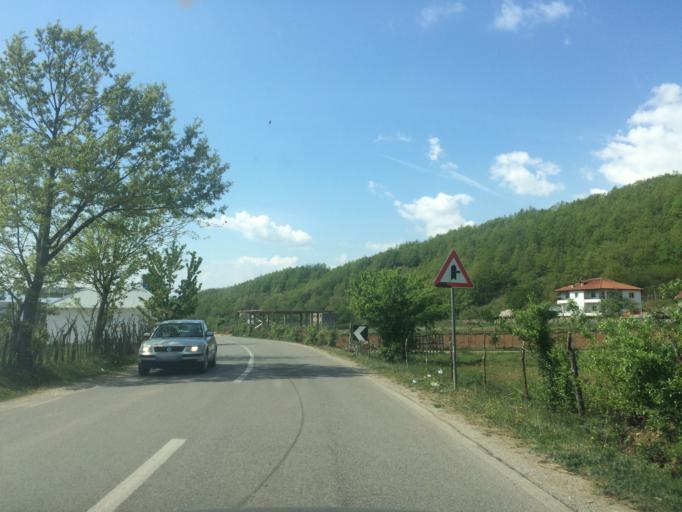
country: AL
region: Kukes
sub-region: Rrethi i Tropojes
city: Llugaj
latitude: 42.3746
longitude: 20.1212
